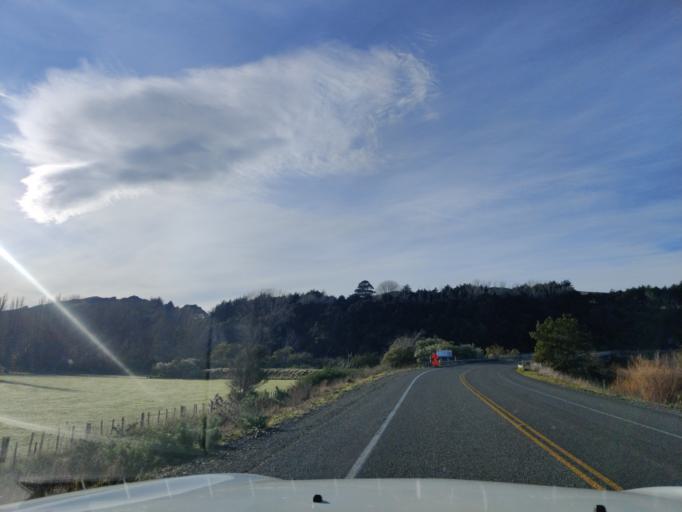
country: NZ
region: Manawatu-Wanganui
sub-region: Palmerston North City
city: Palmerston North
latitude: -40.2807
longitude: 175.7690
